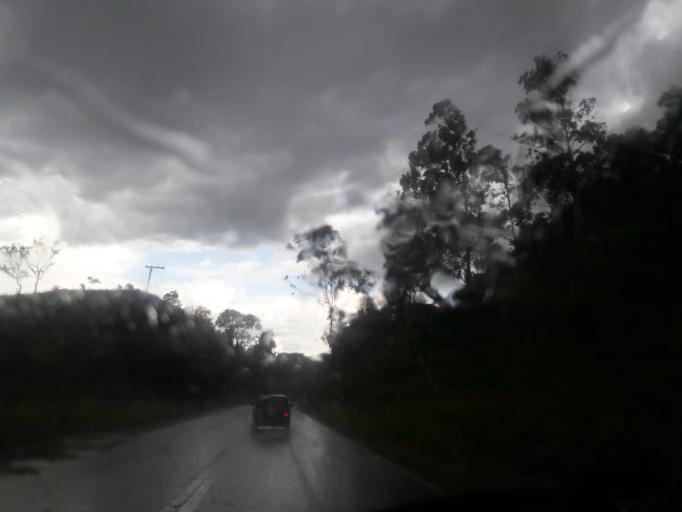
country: BR
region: Sao Paulo
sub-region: Bom Jesus Dos Perdoes
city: Bom Jesus dos Perdoes
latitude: -23.2035
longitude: -46.3909
